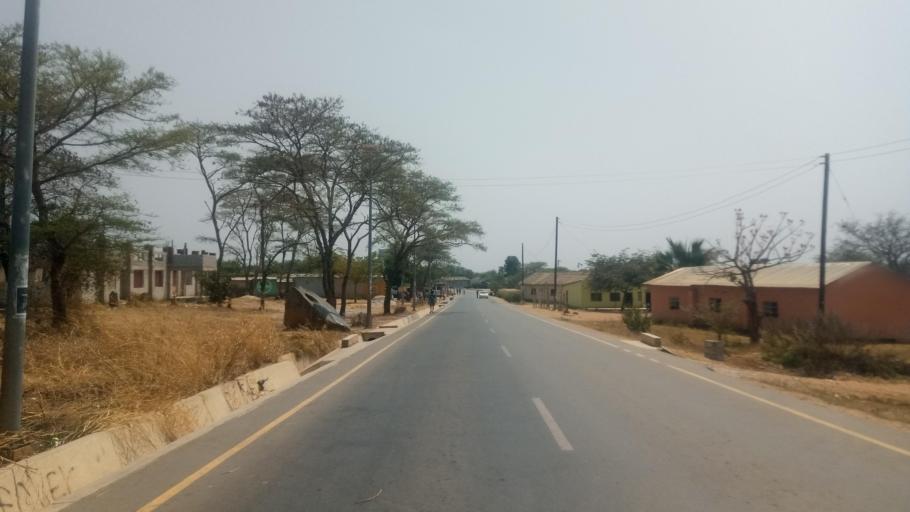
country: ZM
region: Lusaka
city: Lusaka
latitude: -15.4506
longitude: 28.4415
